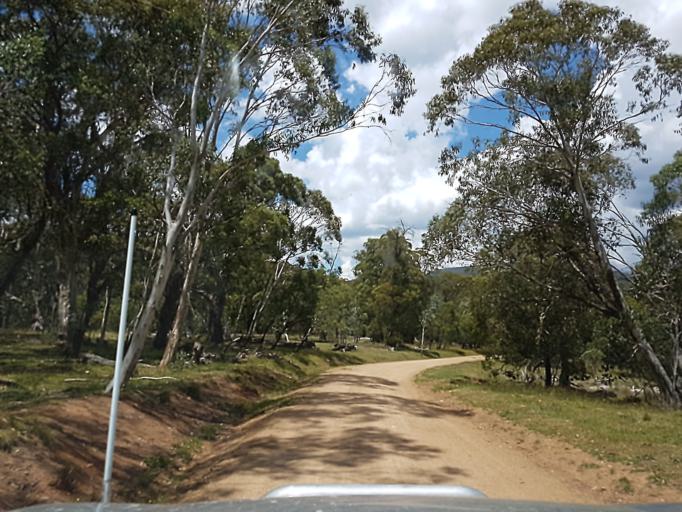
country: AU
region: New South Wales
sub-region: Snowy River
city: Jindabyne
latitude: -36.8932
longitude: 148.0883
